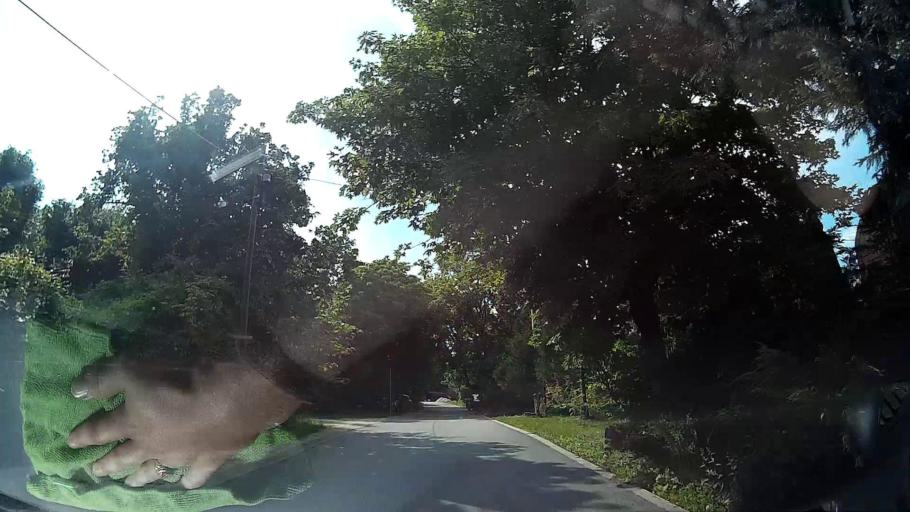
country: HU
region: Pest
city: Budaors
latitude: 47.4865
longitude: 18.9711
